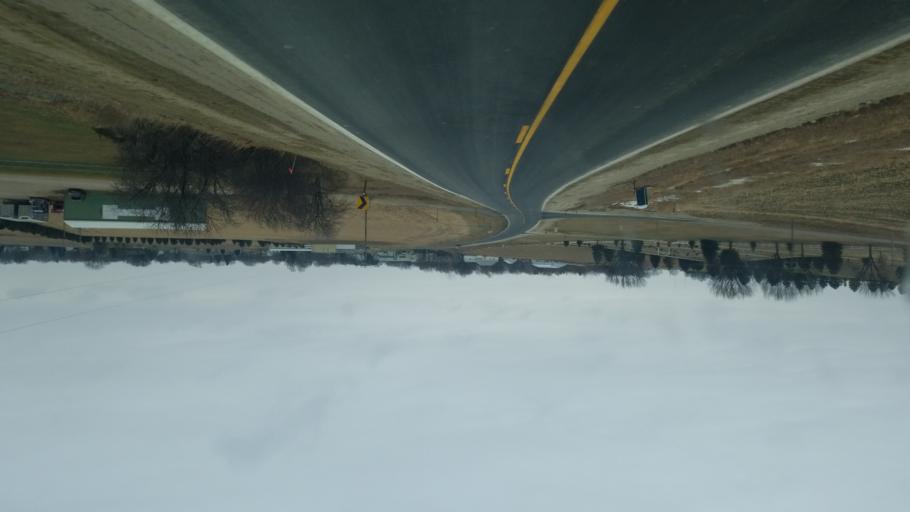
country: US
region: Nebraska
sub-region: Knox County
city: Bloomfield
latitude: 42.5984
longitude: -97.6635
